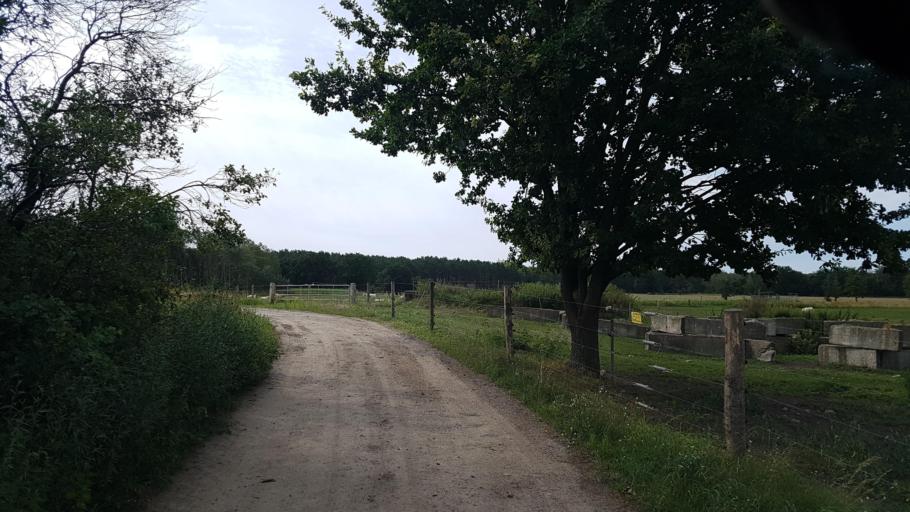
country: DE
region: Brandenburg
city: Drebkau
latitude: 51.6361
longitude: 14.2503
